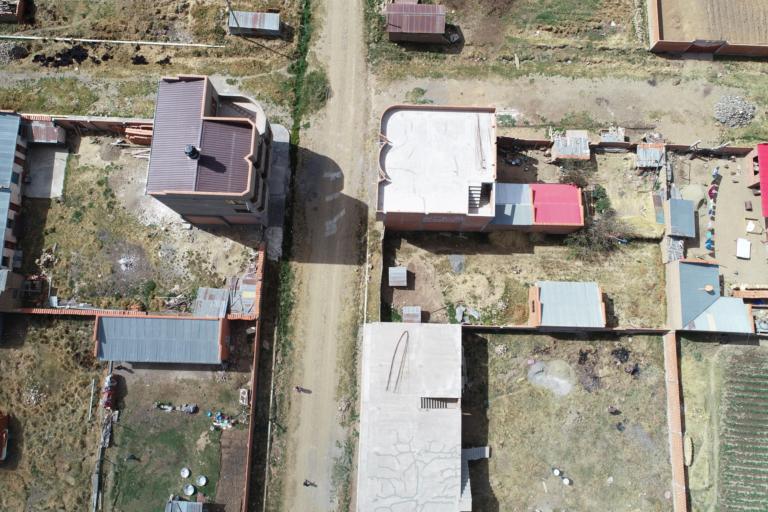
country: BO
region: La Paz
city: Huatajata
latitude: -16.1915
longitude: -68.7433
